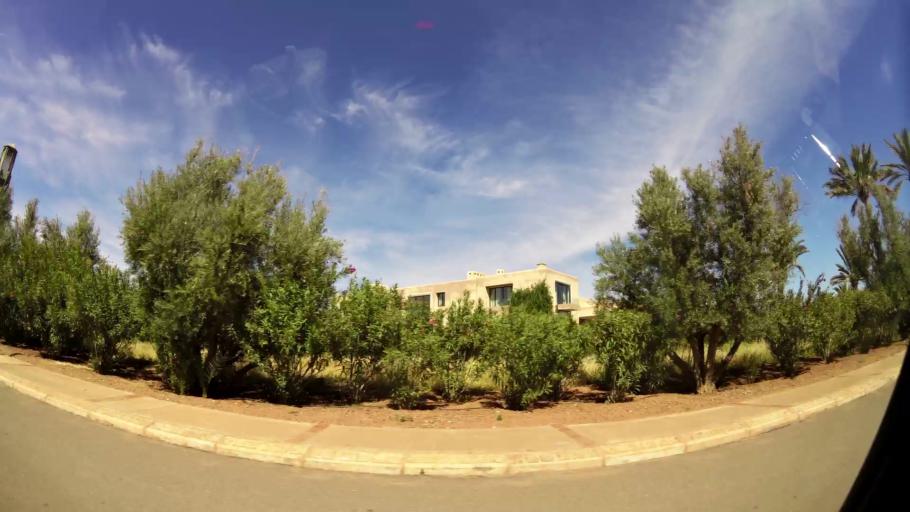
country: MA
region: Marrakech-Tensift-Al Haouz
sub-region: Marrakech
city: Marrakesh
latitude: 31.6129
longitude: -7.9335
